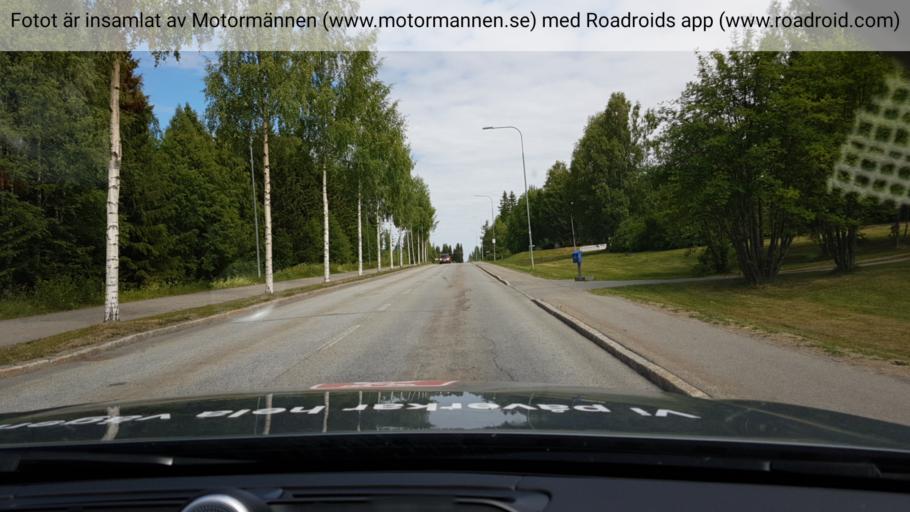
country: SE
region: Jaemtland
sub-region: Stroemsunds Kommun
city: Stroemsund
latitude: 63.8616
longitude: 15.5683
